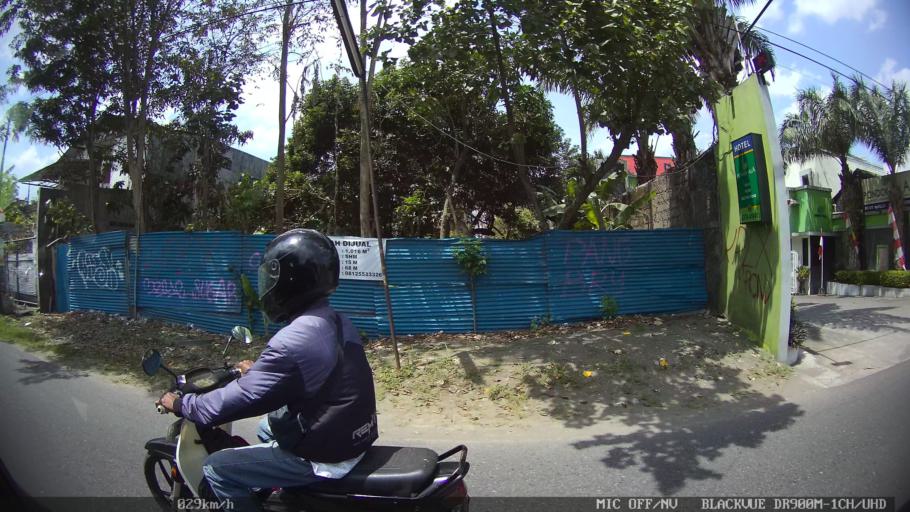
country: ID
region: Daerah Istimewa Yogyakarta
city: Gamping Lor
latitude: -7.8054
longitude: 110.3408
